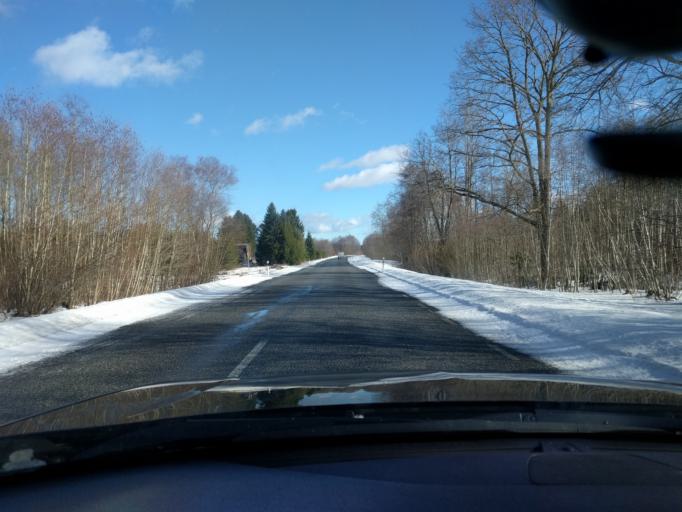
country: EE
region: Harju
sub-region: Raasiku vald
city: Raasiku
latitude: 59.4100
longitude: 25.2212
